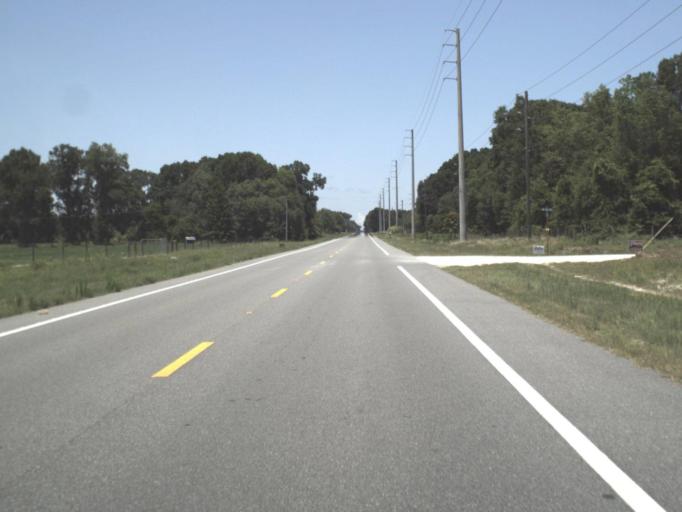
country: US
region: Florida
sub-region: Dixie County
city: Cross City
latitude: 29.6957
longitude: -82.9843
